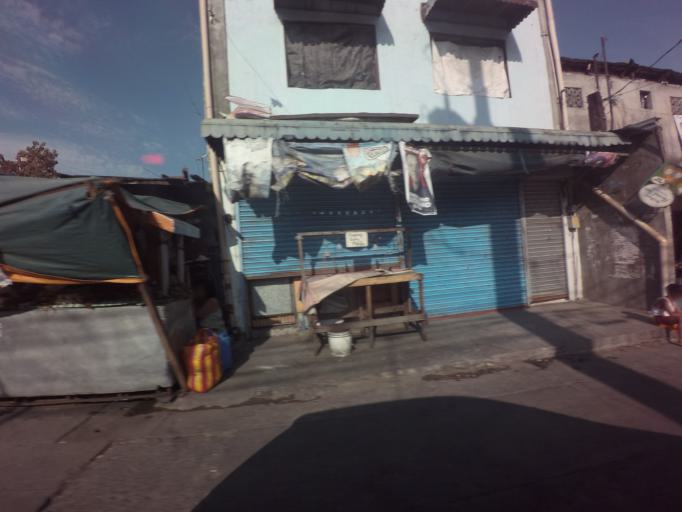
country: PH
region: Calabarzon
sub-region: Province of Rizal
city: Taguig
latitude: 14.4946
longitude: 121.0479
